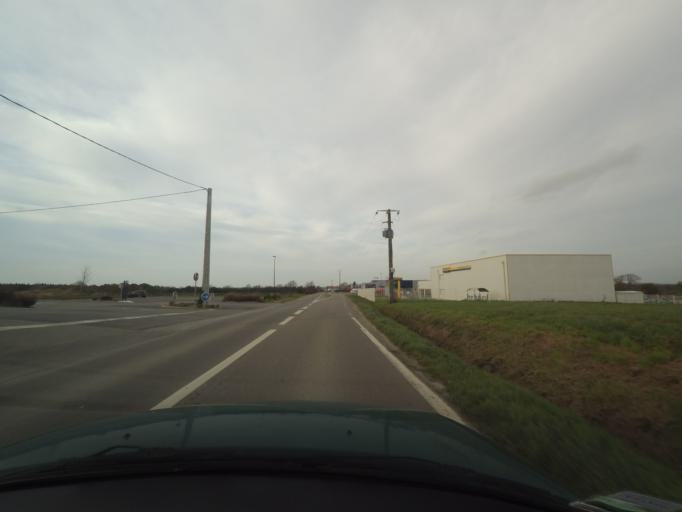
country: FR
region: Pays de la Loire
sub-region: Departement de la Loire-Atlantique
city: Saint-Pere-en-Retz
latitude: 47.1958
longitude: -2.0294
